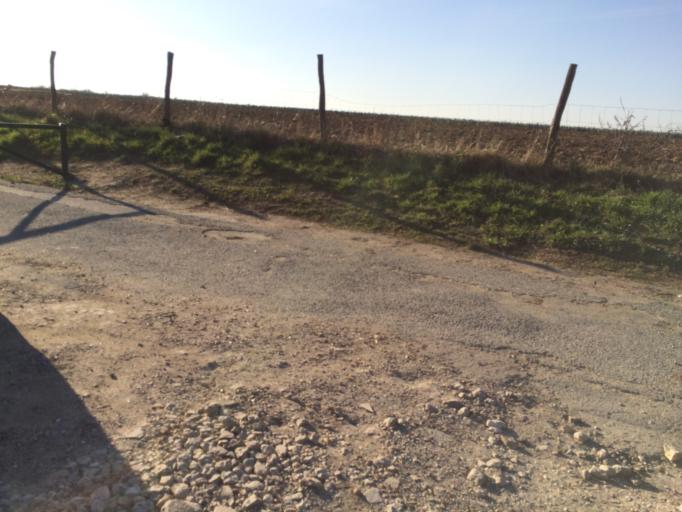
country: FR
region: Ile-de-France
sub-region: Departement de l'Essonne
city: Vauhallan
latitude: 48.7277
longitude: 2.2021
